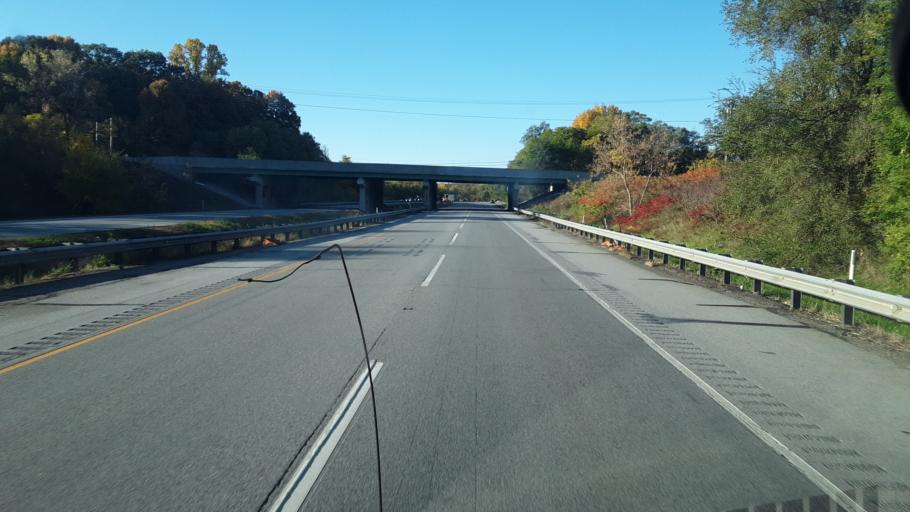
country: US
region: Indiana
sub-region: LaPorte County
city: LaPorte
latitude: 41.6788
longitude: -86.6675
